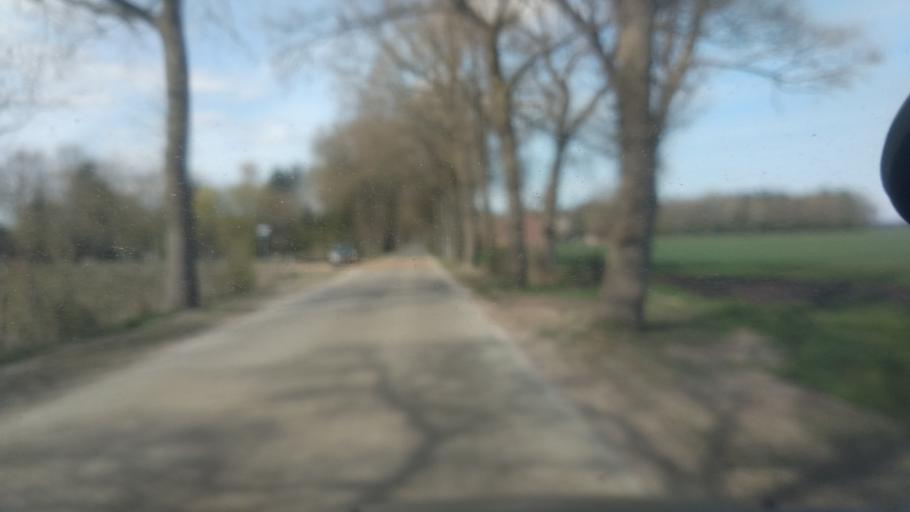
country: NL
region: Drenthe
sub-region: Gemeente Borger-Odoorn
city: Borger
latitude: 52.9529
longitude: 6.8243
